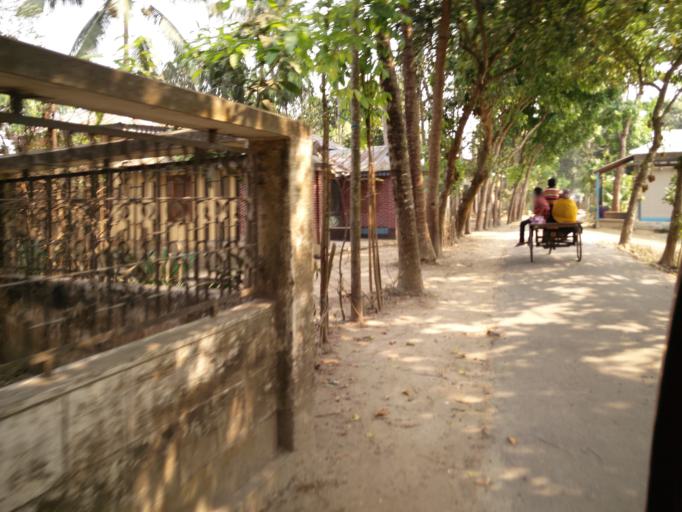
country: BD
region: Dhaka
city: Muktagacha
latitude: 24.9144
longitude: 90.2293
